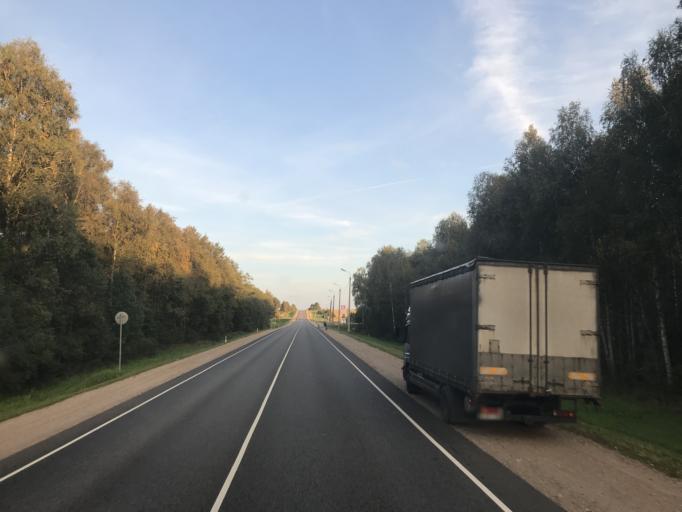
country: RU
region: Smolensk
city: Rudnya
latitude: 54.9850
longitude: 30.9647
